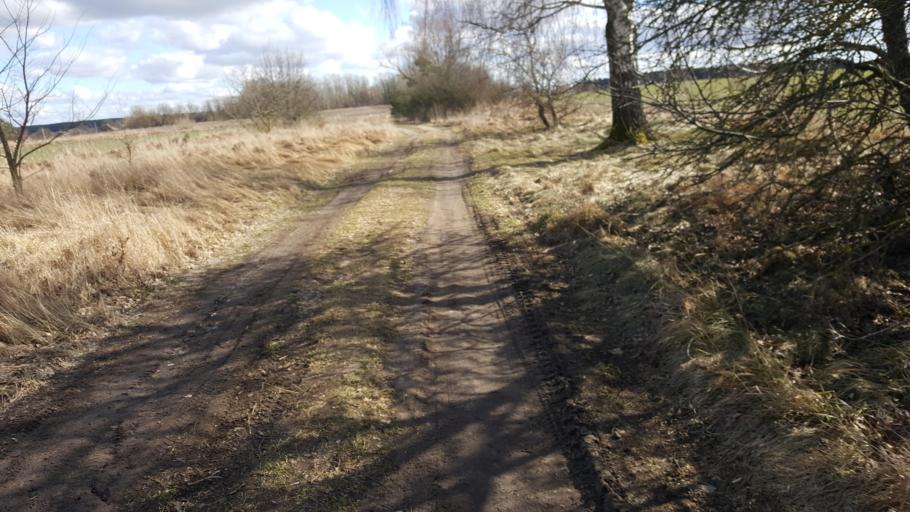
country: BY
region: Brest
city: Kamyanyets
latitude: 52.3914
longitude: 23.8774
